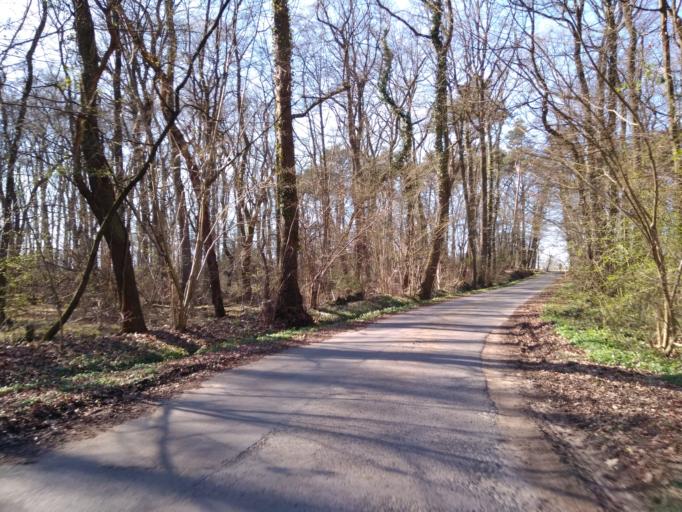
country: DE
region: North Rhine-Westphalia
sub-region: Regierungsbezirk Dusseldorf
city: Schermbeck
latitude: 51.6553
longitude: 6.8631
